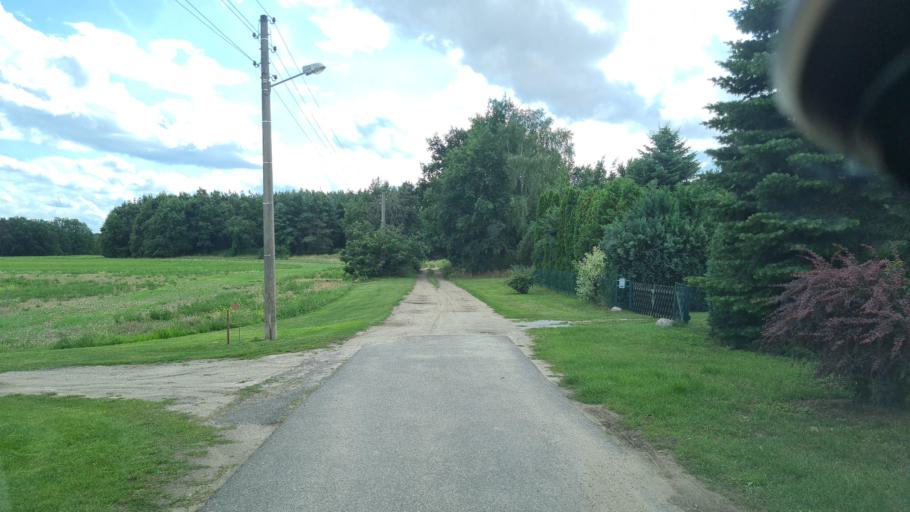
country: DE
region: Brandenburg
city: Drebkau
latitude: 51.6331
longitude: 14.2825
